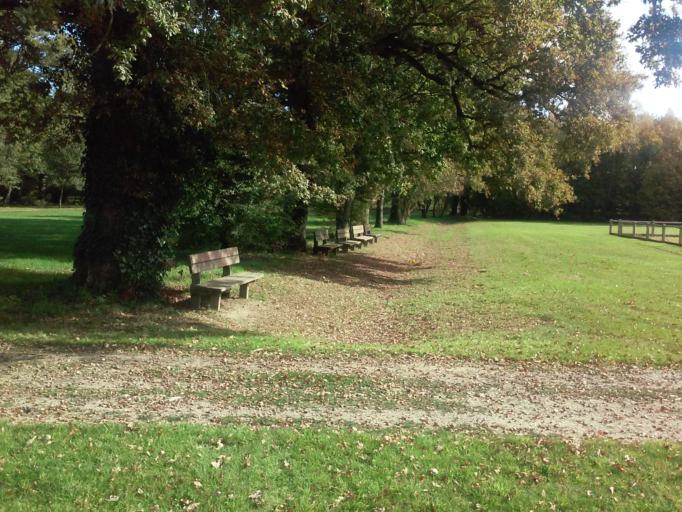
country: FR
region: Pays de la Loire
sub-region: Departement de la Vendee
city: Saint-Andre-Treize-Voies
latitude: 46.8789
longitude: -1.4045
